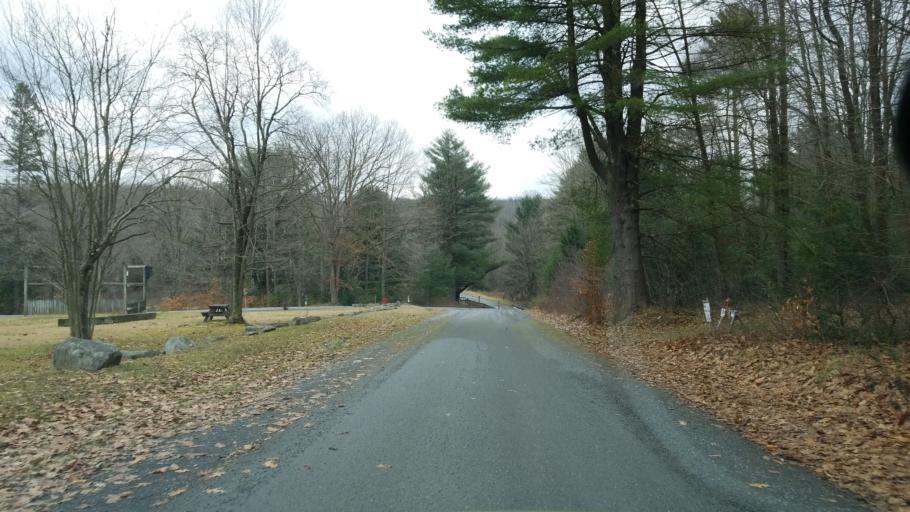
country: US
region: Pennsylvania
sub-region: Clearfield County
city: Clearfield
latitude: 41.1932
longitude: -78.5095
